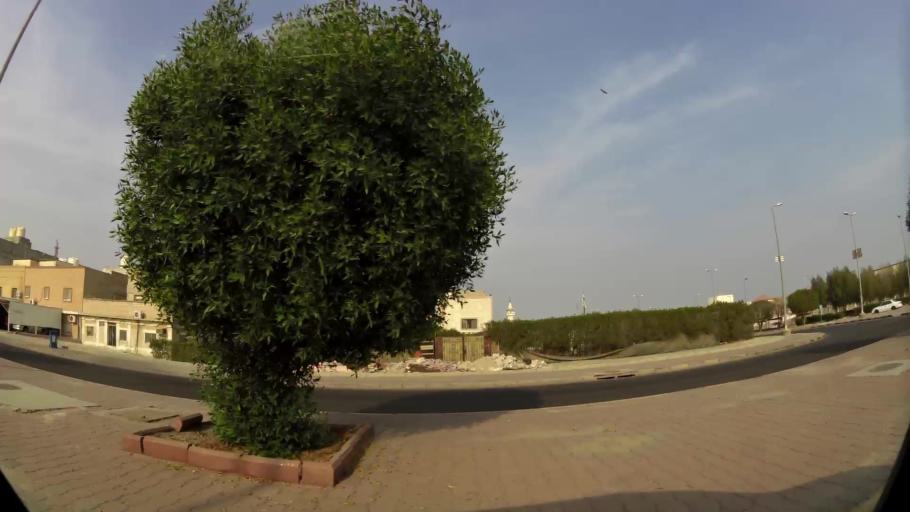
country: KW
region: Mubarak al Kabir
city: Sabah as Salim
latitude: 29.2478
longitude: 48.0543
